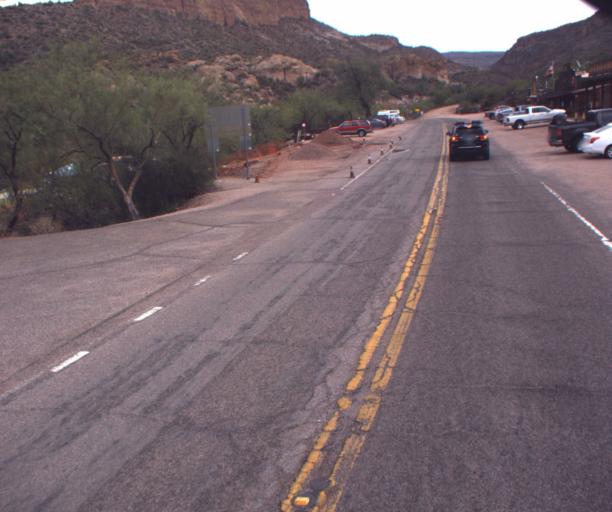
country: US
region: Arizona
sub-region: Pinal County
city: Apache Junction
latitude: 33.5259
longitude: -111.3909
